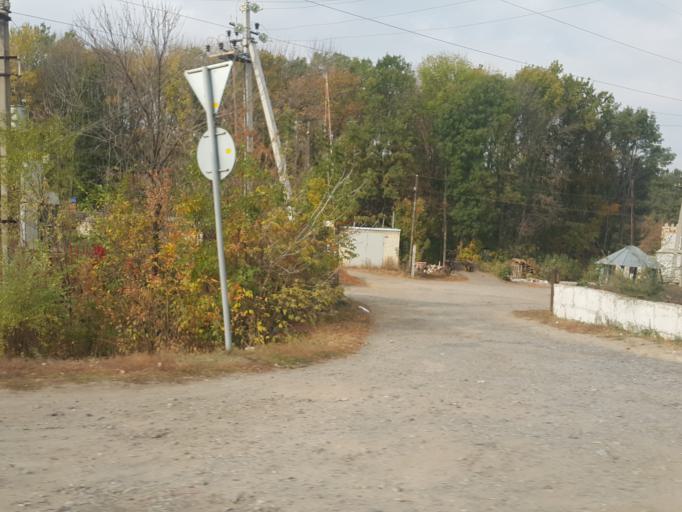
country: RU
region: Tambov
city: Bokino
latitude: 52.6598
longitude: 41.4479
